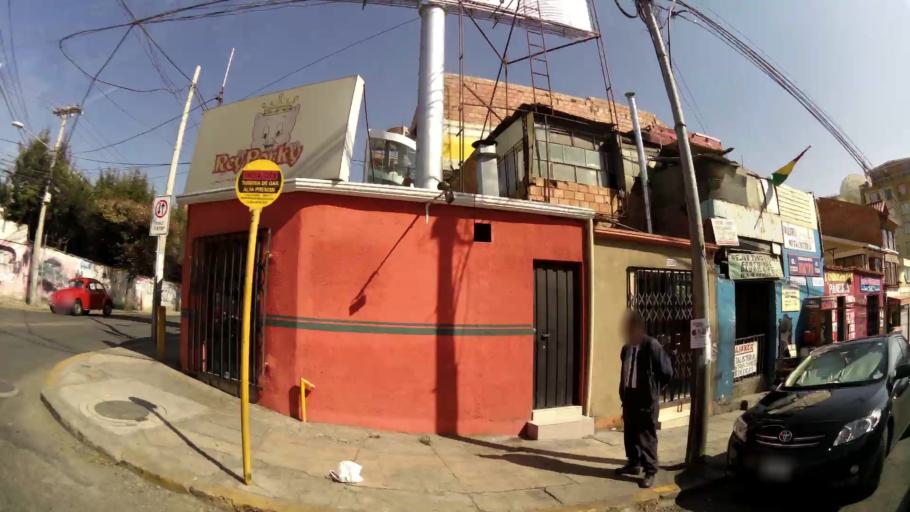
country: BO
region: La Paz
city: La Paz
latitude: -16.5364
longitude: -68.0756
